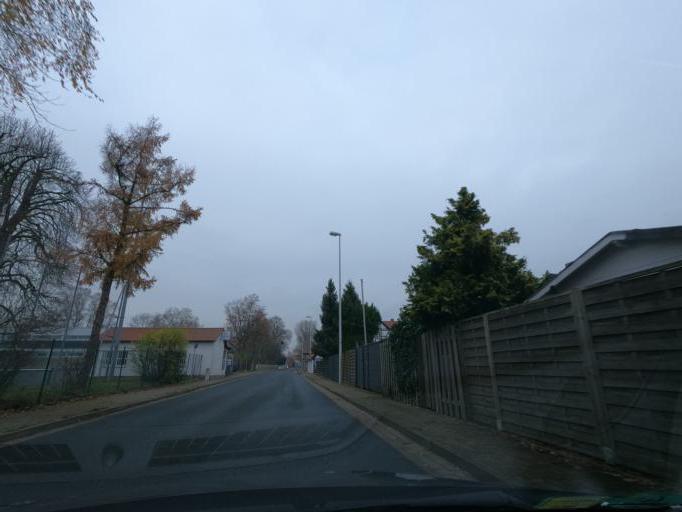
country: DE
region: Lower Saxony
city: Wolfenbuettel
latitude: 52.1933
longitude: 10.5878
